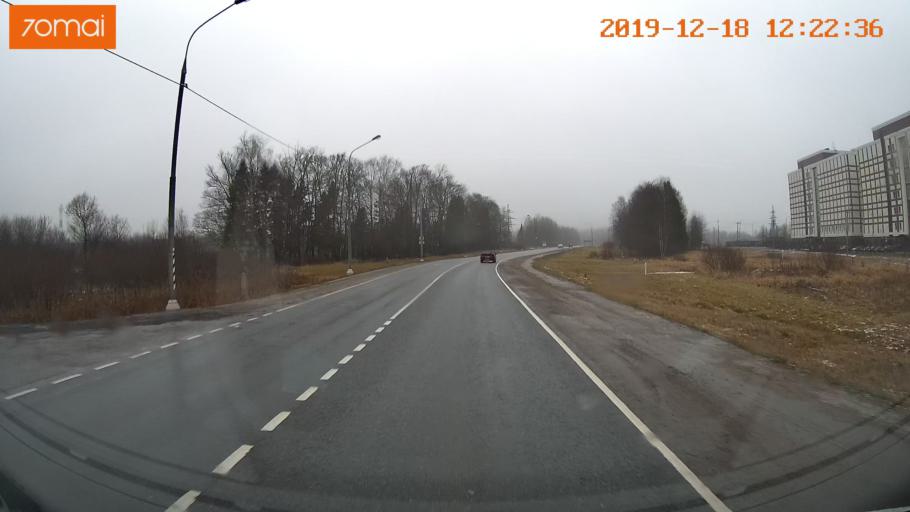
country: RU
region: Moskovskaya
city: Novopetrovskoye
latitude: 56.0071
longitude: 36.4819
